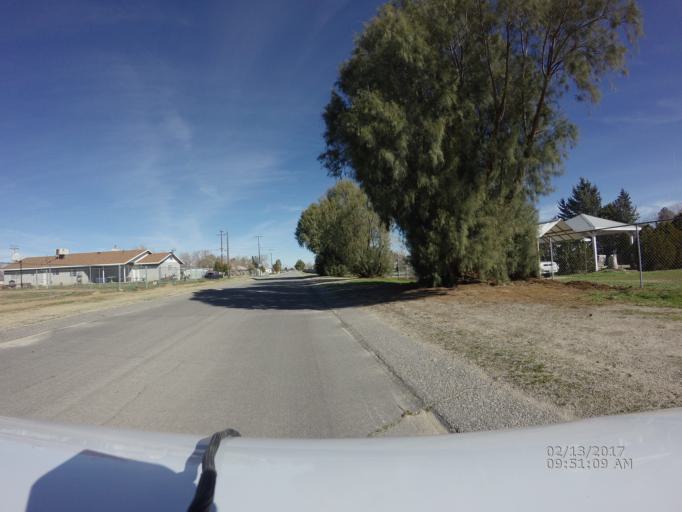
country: US
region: California
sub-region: Los Angeles County
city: Littlerock
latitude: 34.5387
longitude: -117.9713
